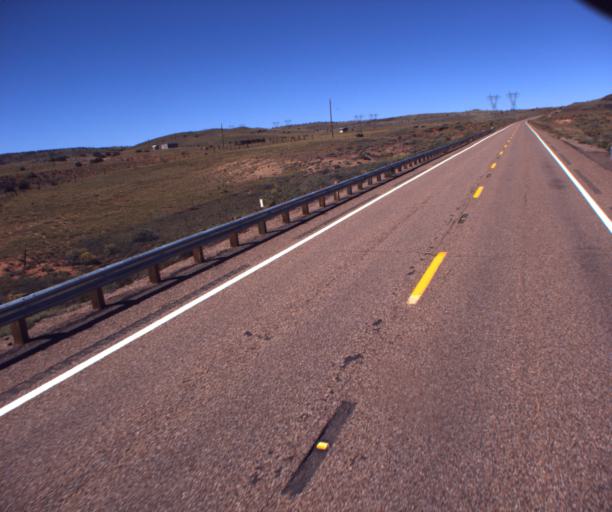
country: US
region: Arizona
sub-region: Apache County
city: Saint Johns
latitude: 34.5466
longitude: -109.4809
